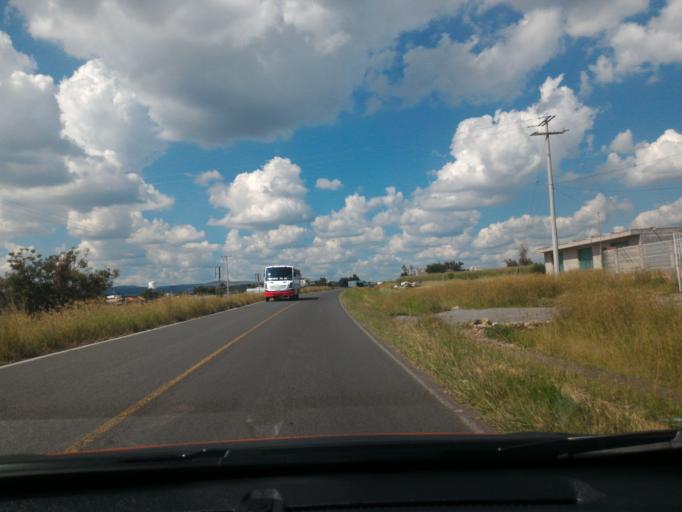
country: MX
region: Guanajuato
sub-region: Penjamo
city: Estacion la Piedad
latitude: 20.4078
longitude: -101.9982
